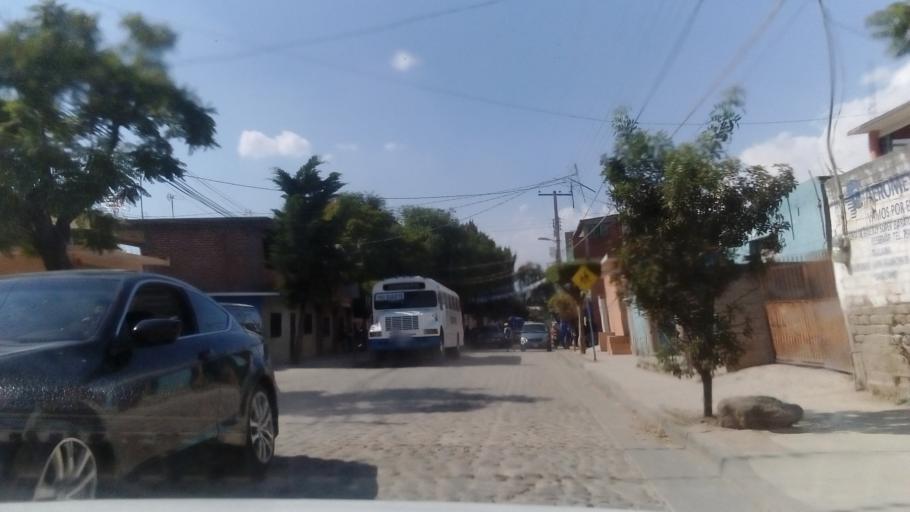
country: MX
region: Guanajuato
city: Duarte
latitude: 21.0847
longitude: -101.5179
